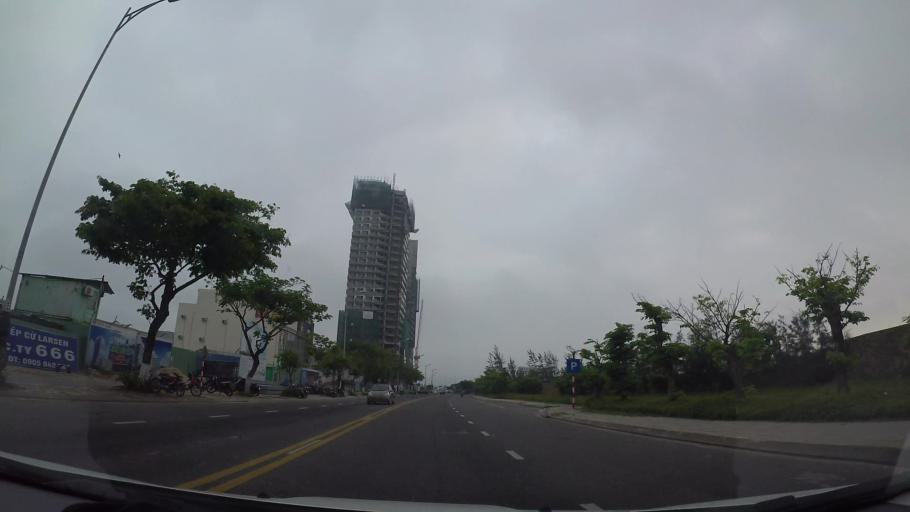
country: VN
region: Da Nang
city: Son Tra
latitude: 16.0786
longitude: 108.2459
